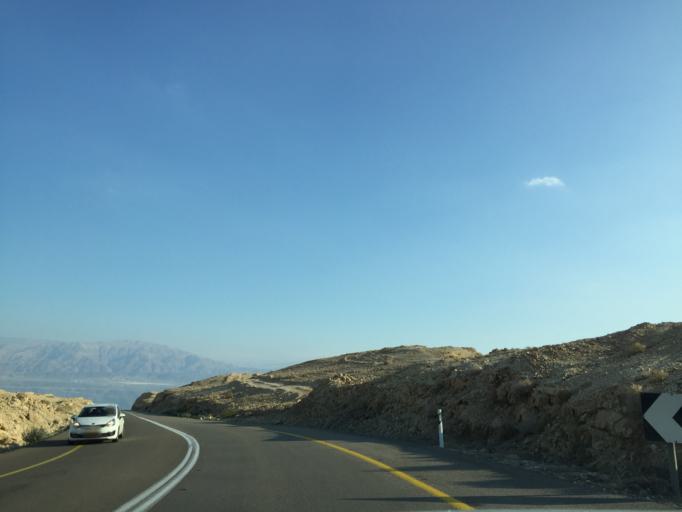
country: IL
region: Southern District
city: `En Boqeq
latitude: 31.1600
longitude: 35.3293
